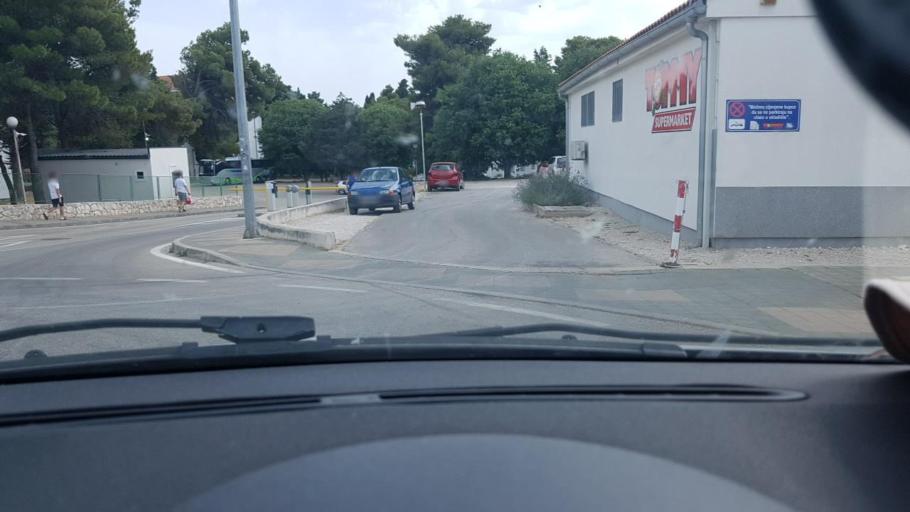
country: HR
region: Sibensko-Kniniska
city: Vodice
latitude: 43.7555
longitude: 15.7882
